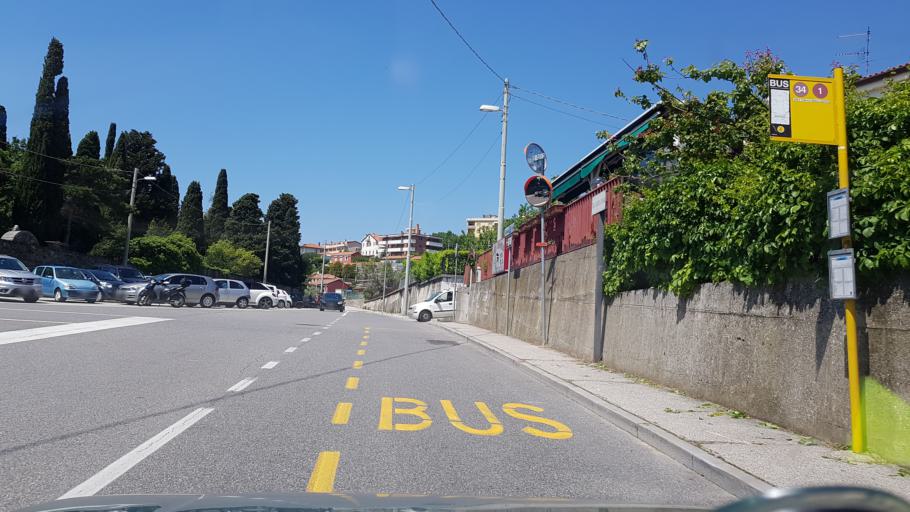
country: IT
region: Friuli Venezia Giulia
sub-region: Provincia di Trieste
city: Trieste
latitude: 45.6329
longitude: 13.7957
